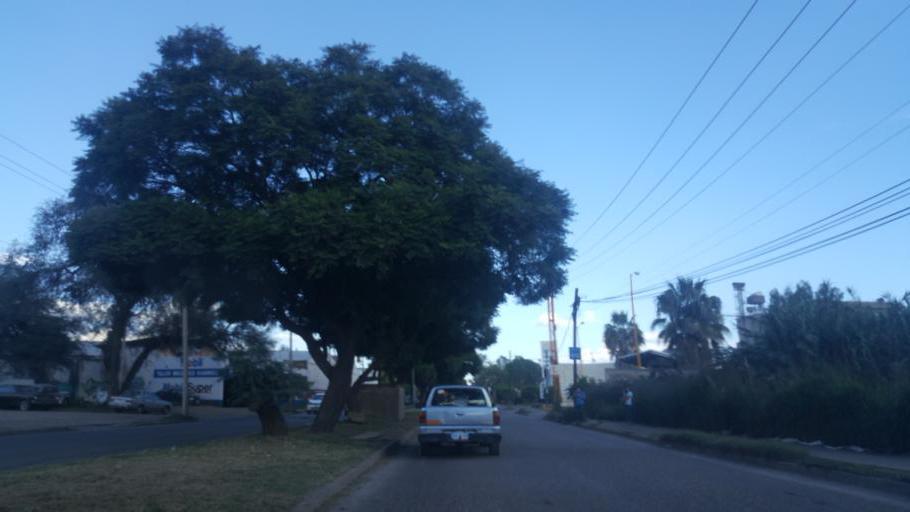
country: MX
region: Guanajuato
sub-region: Leon
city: San Jose de Duran (Los Troncoso)
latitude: 21.0950
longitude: -101.6945
